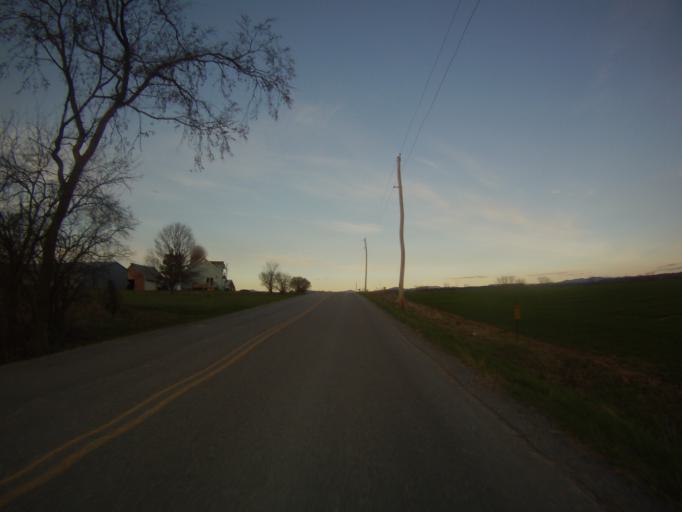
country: US
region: Vermont
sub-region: Addison County
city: Middlebury (village)
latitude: 44.0181
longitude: -73.2505
